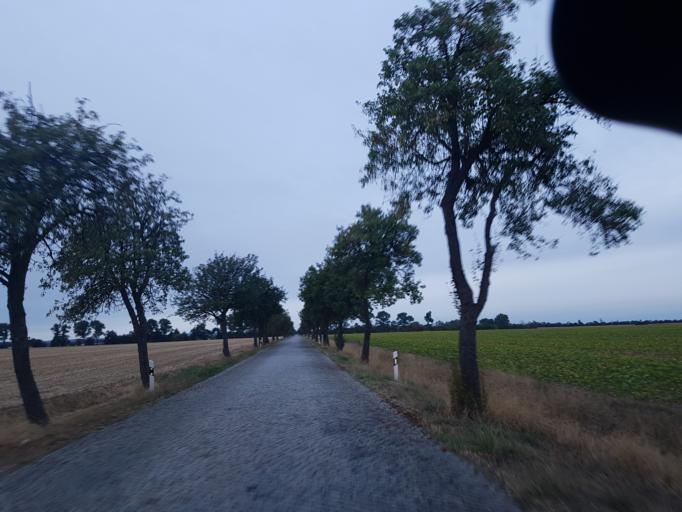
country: DE
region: Brandenburg
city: Muhlberg
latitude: 51.4962
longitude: 13.2205
